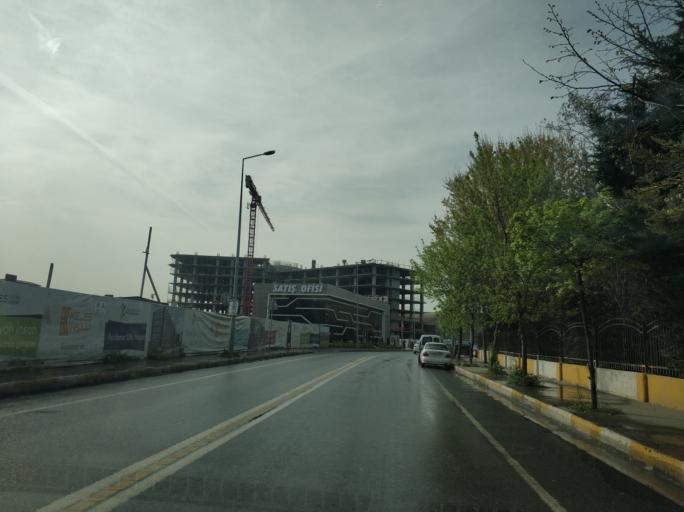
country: TR
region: Istanbul
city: Bahcelievler
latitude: 41.0017
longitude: 28.8096
